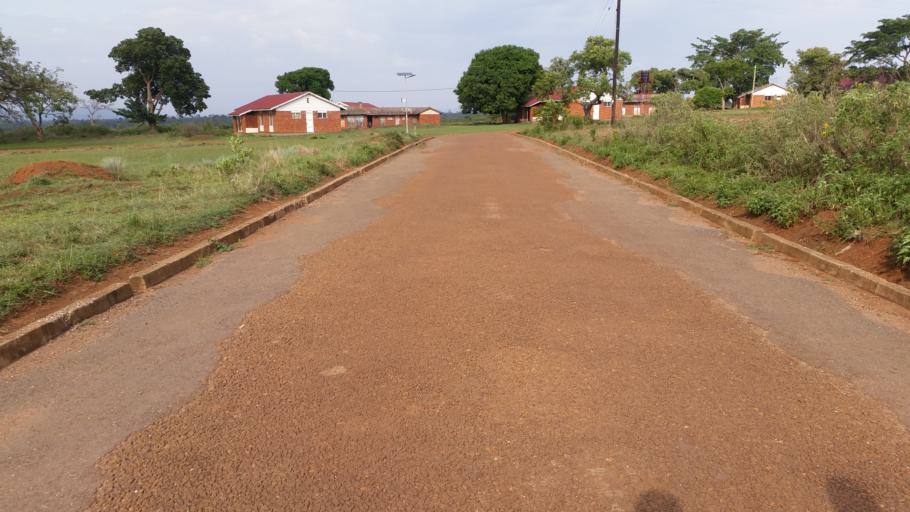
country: UG
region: Eastern Region
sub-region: Busia District
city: Busia
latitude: 0.5462
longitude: 34.0240
